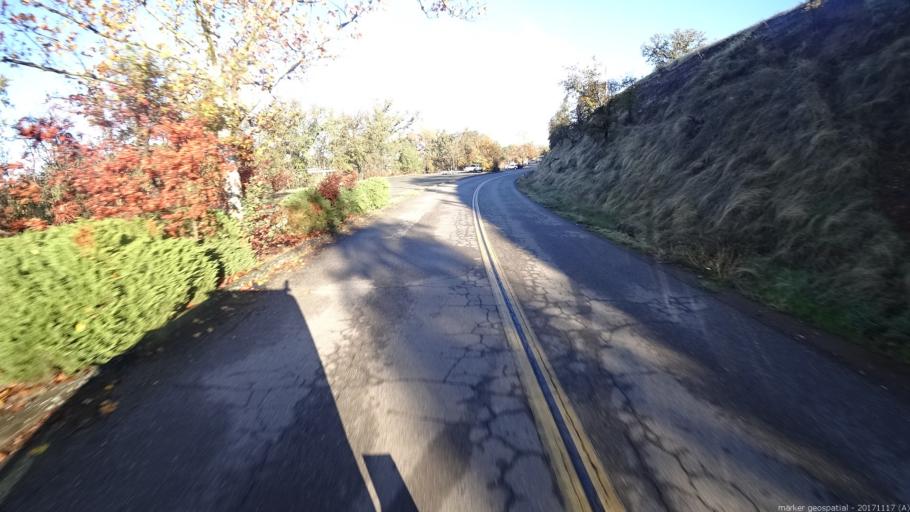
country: US
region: California
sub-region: Shasta County
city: Cottonwood
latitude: 40.4160
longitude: -122.1923
